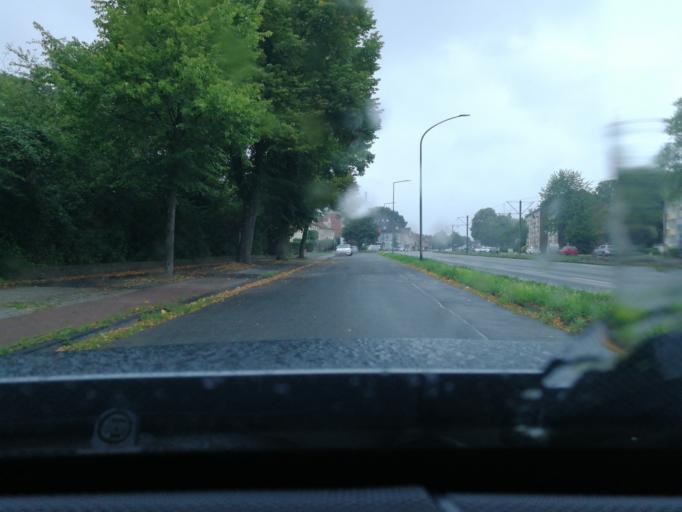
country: DE
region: North Rhine-Westphalia
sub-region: Regierungsbezirk Dusseldorf
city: Dinslaken
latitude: 51.5359
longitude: 6.7401
